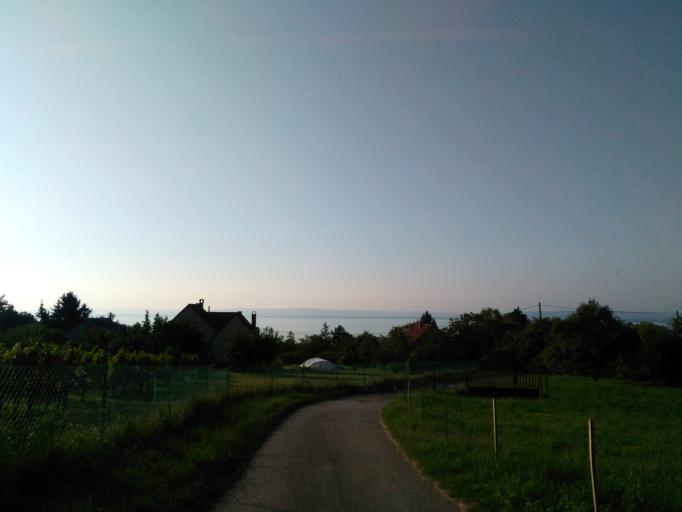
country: HU
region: Veszprem
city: Zanka
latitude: 46.8522
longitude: 17.6503
